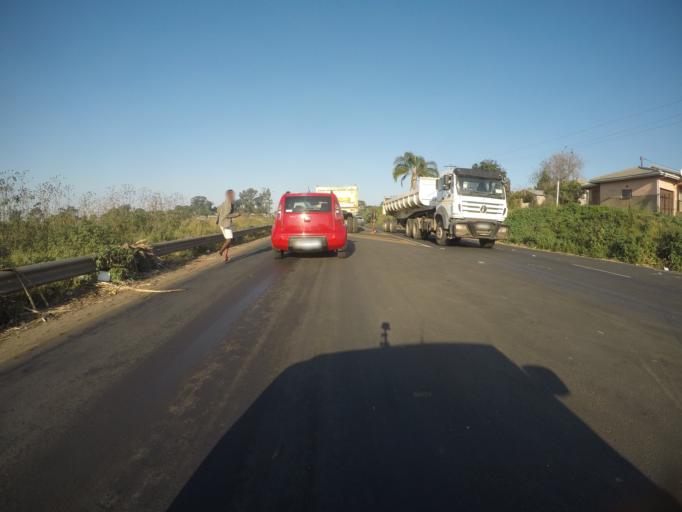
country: ZA
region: KwaZulu-Natal
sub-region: iLembe District Municipality
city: Stanger
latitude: -29.4120
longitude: 31.2444
